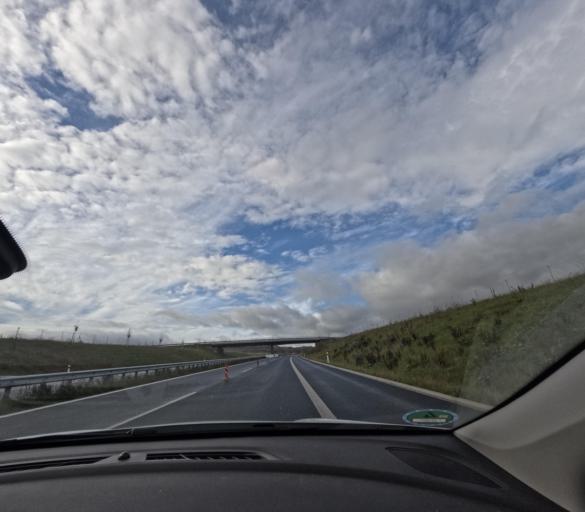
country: CZ
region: Ustecky
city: Lubenec
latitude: 50.1339
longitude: 13.2974
